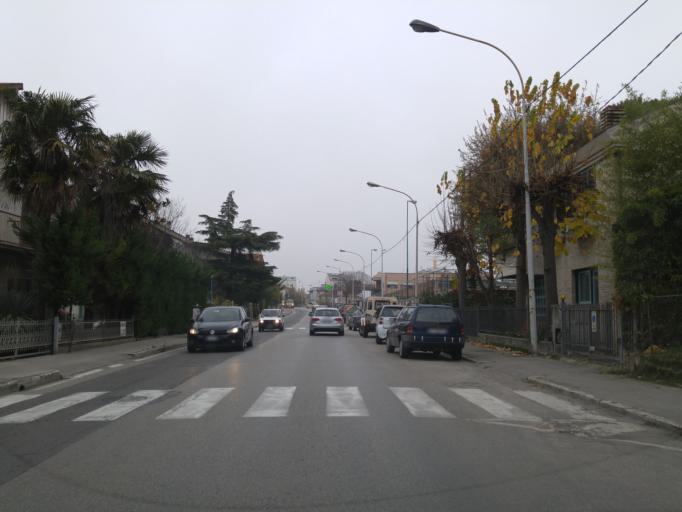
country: IT
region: Emilia-Romagna
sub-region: Provincia di Rimini
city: Cattolica
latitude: 43.9634
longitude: 12.7309
